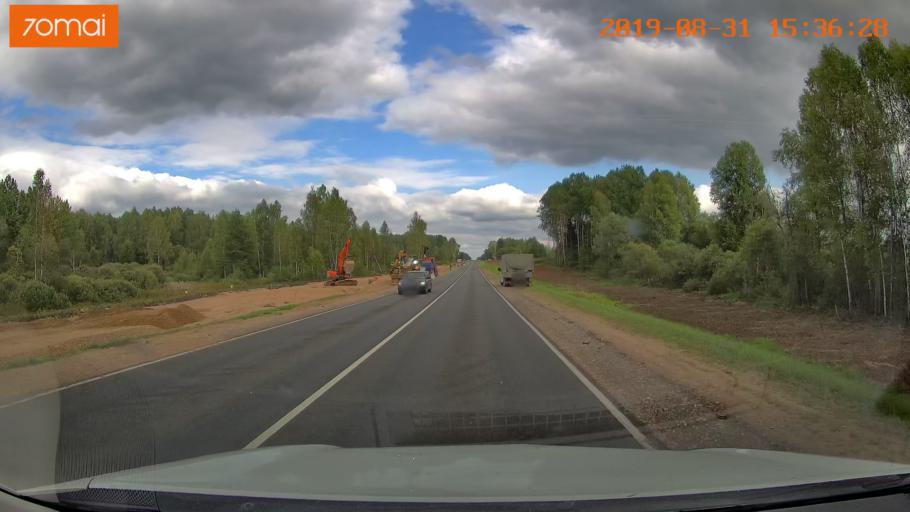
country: RU
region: Kaluga
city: Mosal'sk
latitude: 54.6115
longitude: 34.7599
